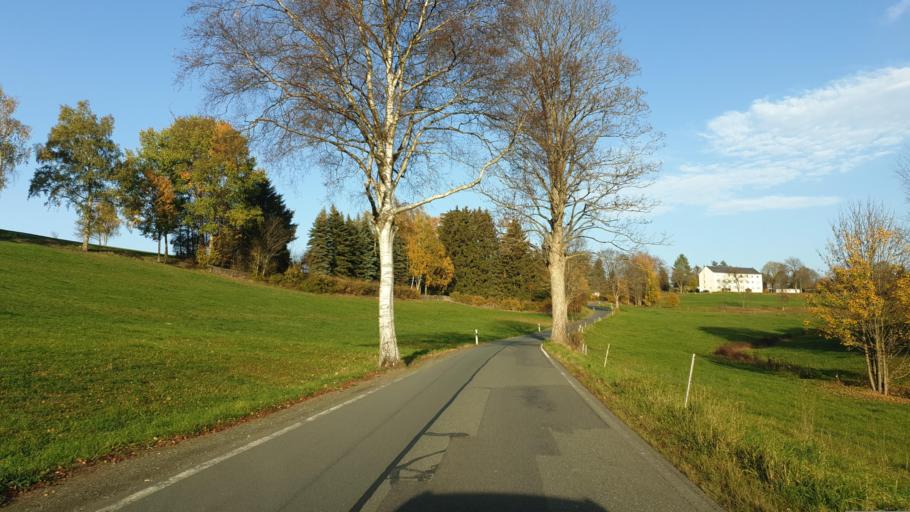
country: DE
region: Saxony
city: Markneukirchen
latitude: 50.2703
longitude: 12.3172
